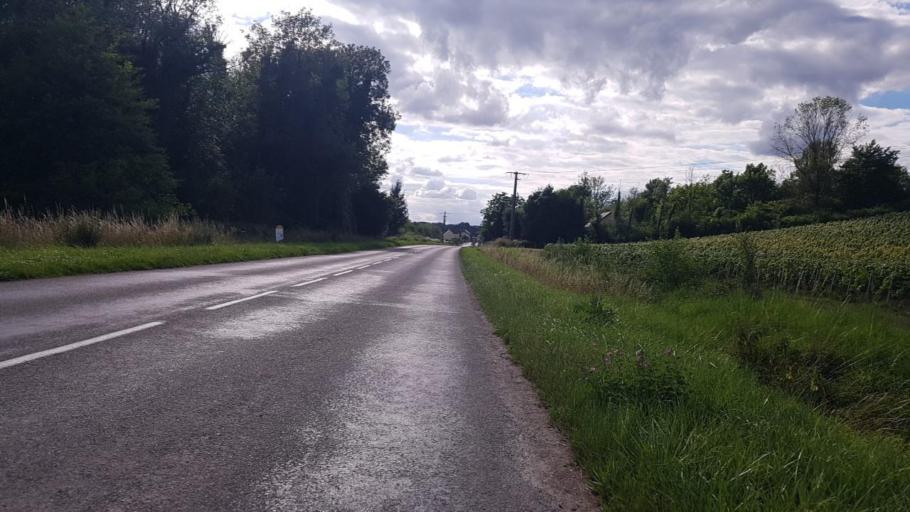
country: FR
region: Picardie
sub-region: Departement de l'Aisne
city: Brasles
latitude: 49.0467
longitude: 3.4374
